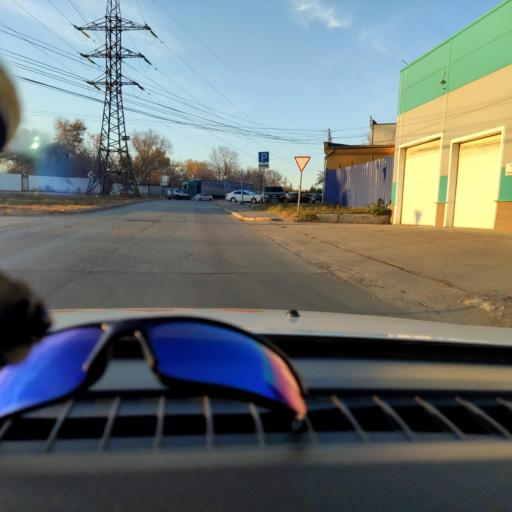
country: RU
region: Samara
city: Samara
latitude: 53.1843
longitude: 50.1729
